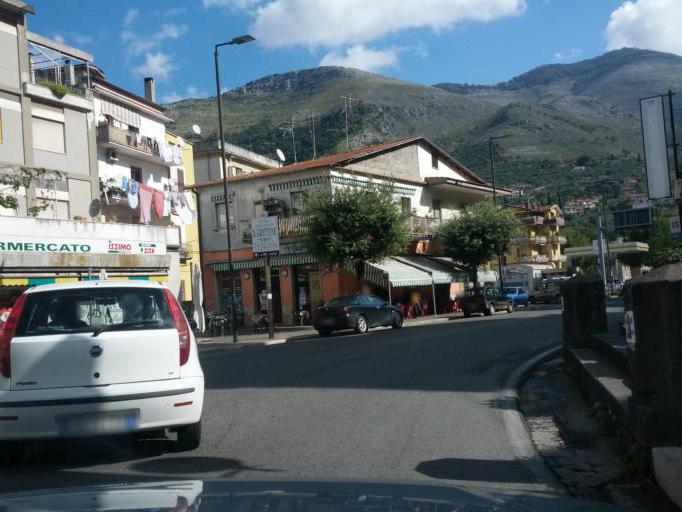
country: IT
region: Latium
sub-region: Provincia di Latina
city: Itri
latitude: 41.2904
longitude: 13.5319
